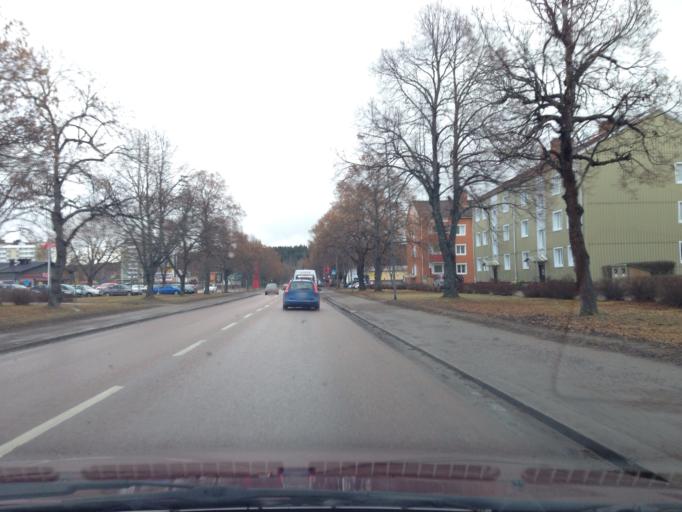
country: SE
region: Dalarna
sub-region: Ludvika Kommun
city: Ludvika
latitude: 60.1502
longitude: 15.2046
